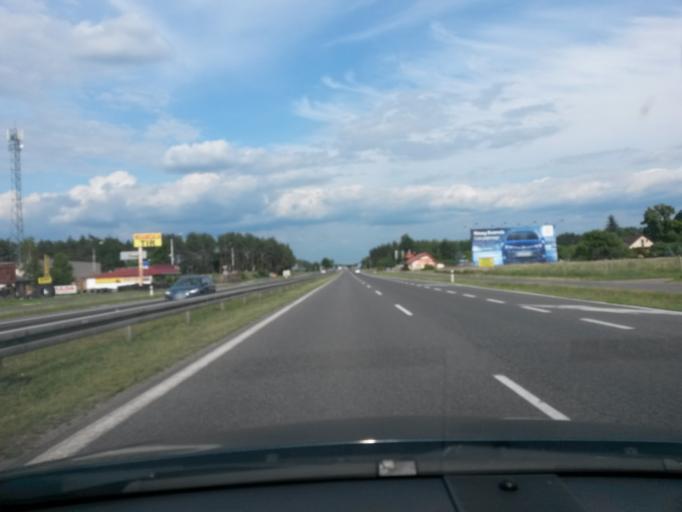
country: PL
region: Masovian Voivodeship
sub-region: Powiat zyrardowski
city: Radziejowice
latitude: 52.0040
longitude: 20.5771
